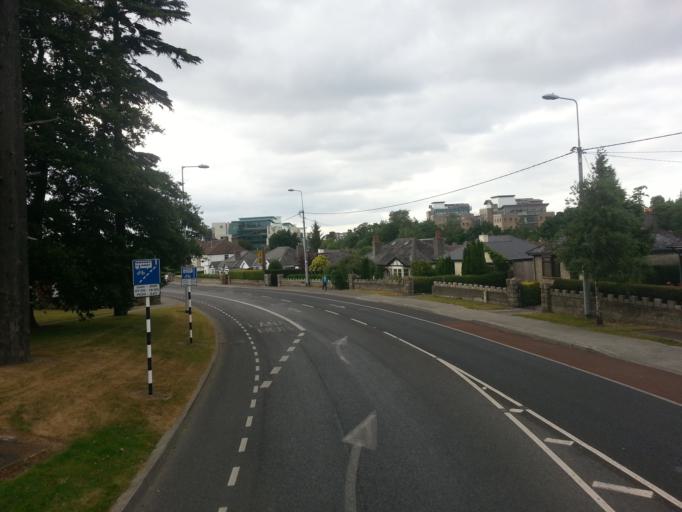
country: IE
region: Leinster
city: Balally
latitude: 53.2833
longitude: -6.2344
